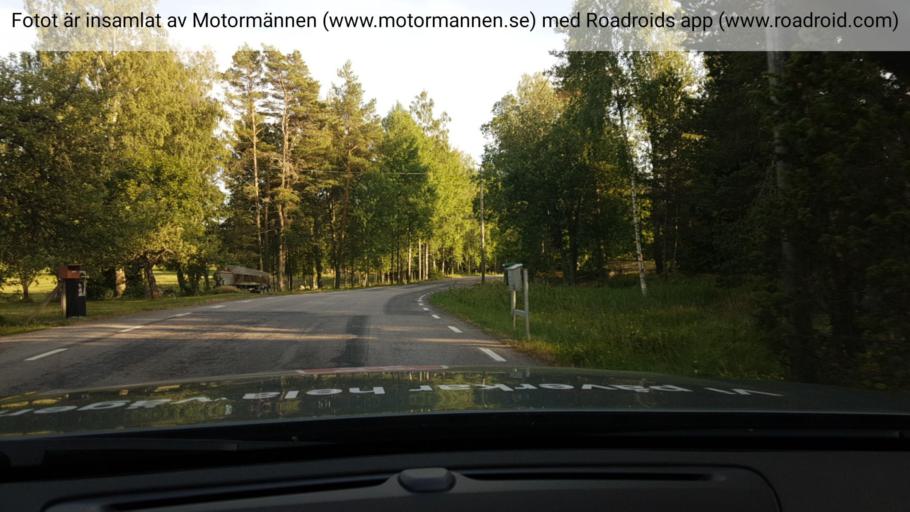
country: SE
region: Uppsala
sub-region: Osthammars Kommun
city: Gimo
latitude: 59.9949
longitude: 18.0595
